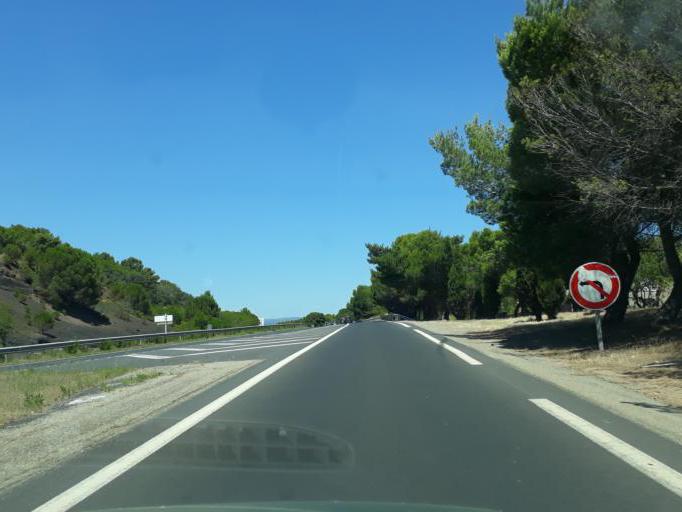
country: FR
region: Languedoc-Roussillon
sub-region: Departement de l'Herault
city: Le Cap d'Agde
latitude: 43.2961
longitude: 3.5064
